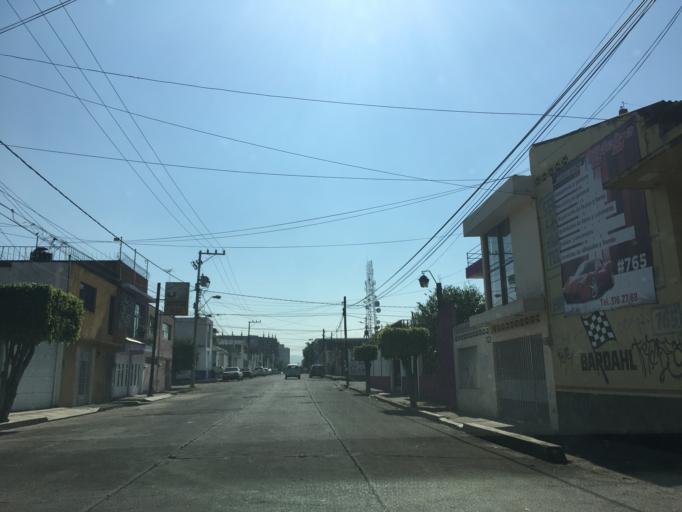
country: MX
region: Michoacan
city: Morelia
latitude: 19.6997
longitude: -101.2143
